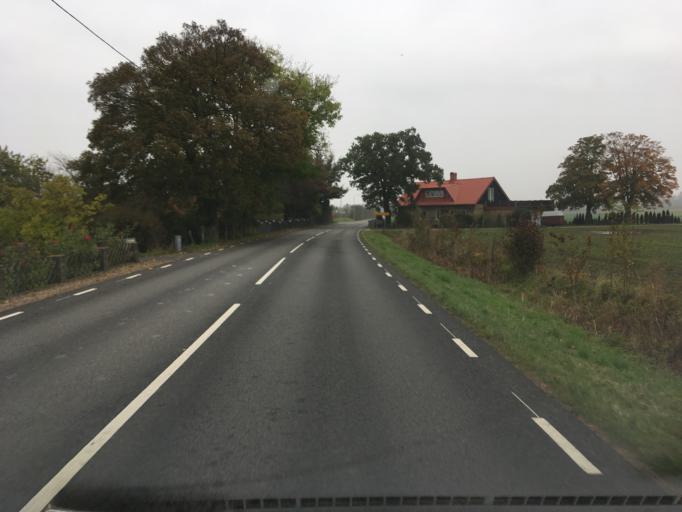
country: SE
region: Skane
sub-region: Lunds Kommun
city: Lund
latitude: 55.7397
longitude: 13.1984
